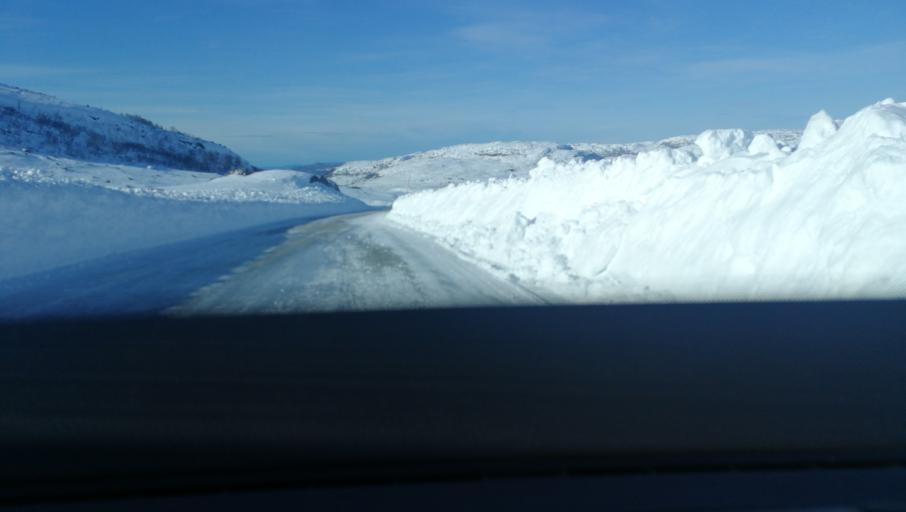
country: NO
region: Rogaland
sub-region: Hjelmeland
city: Hjelmelandsvagen
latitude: 59.1004
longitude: 6.3876
